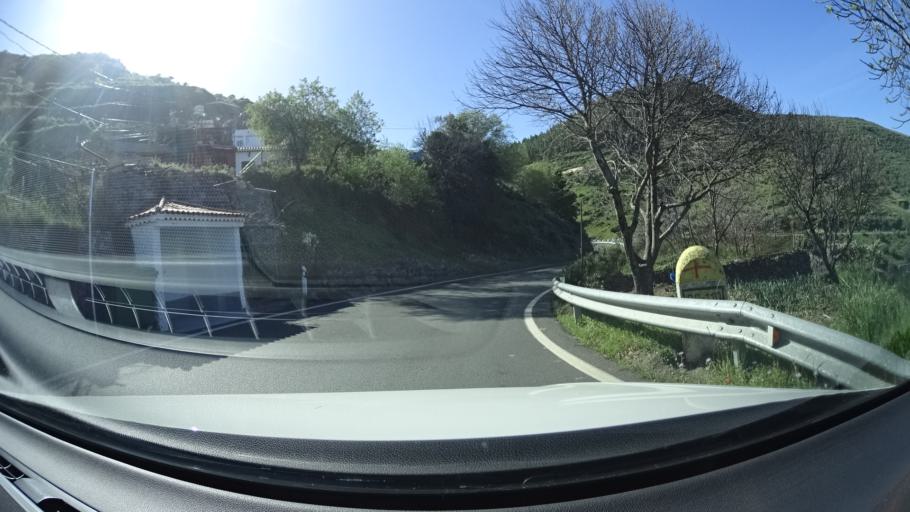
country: ES
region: Canary Islands
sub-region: Provincia de Las Palmas
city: Artenara
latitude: 28.0254
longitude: -15.6343
